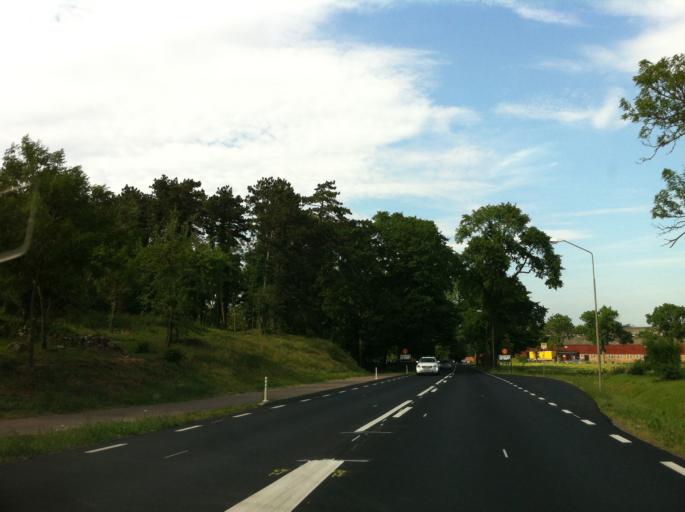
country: SE
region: Kalmar
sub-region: Borgholms Kommun
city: Borgholm
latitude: 56.8682
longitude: 16.6582
